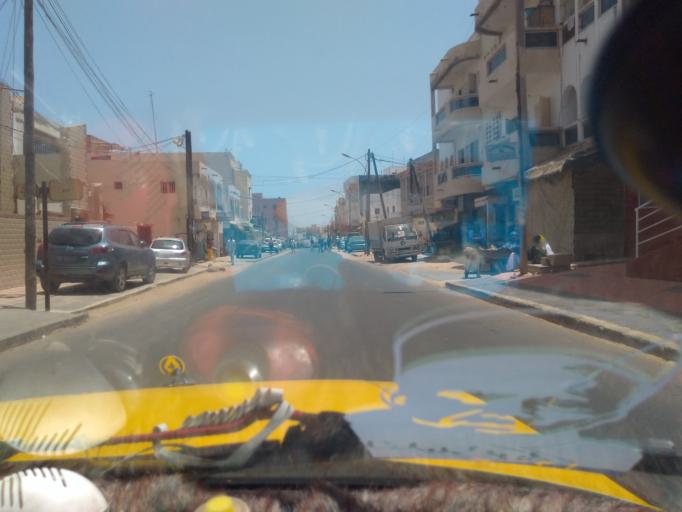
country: SN
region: Dakar
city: Grand Dakar
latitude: 14.7570
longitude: -17.4666
